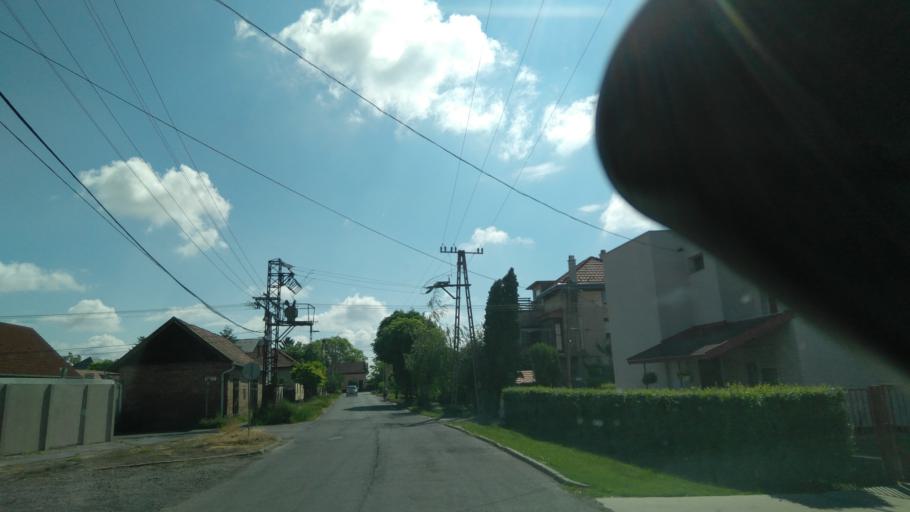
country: HU
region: Bekes
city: Bekes
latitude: 46.7766
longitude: 21.1321
